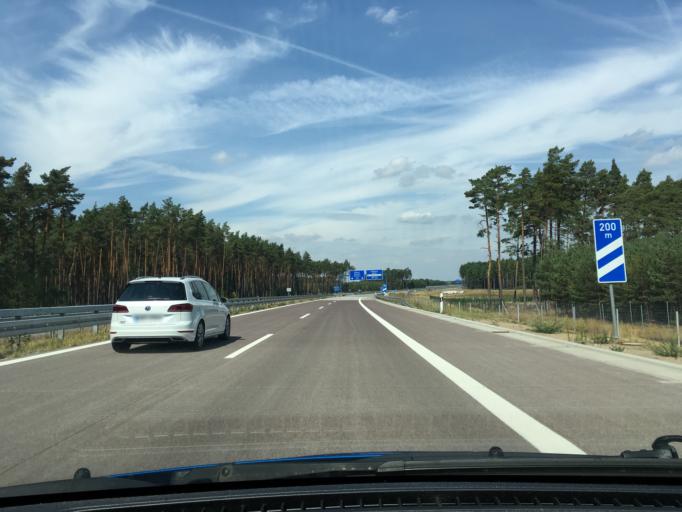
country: DE
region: Mecklenburg-Vorpommern
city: Gross Laasch
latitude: 53.4142
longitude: 11.5248
